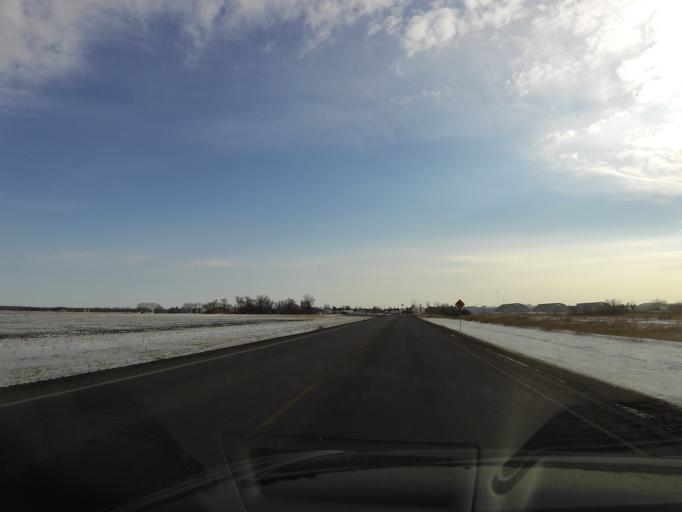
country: US
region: North Dakota
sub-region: Walsh County
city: Grafton
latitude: 48.5775
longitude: -97.1787
